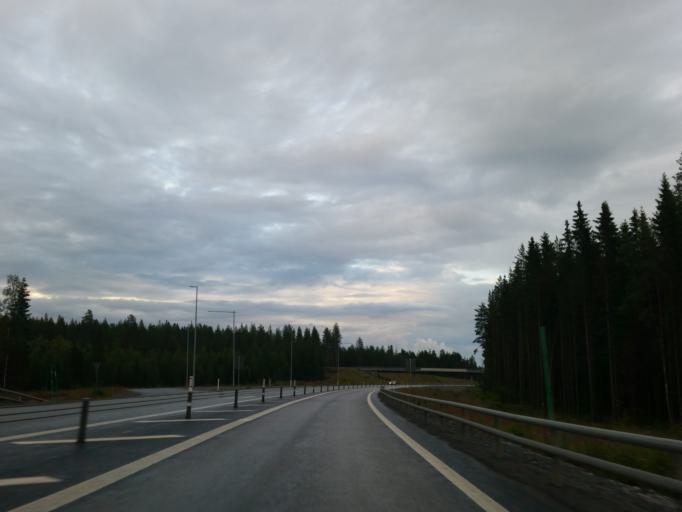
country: SE
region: Vaesterbotten
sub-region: Umea Kommun
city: Umea
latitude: 63.8539
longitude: 20.2809
